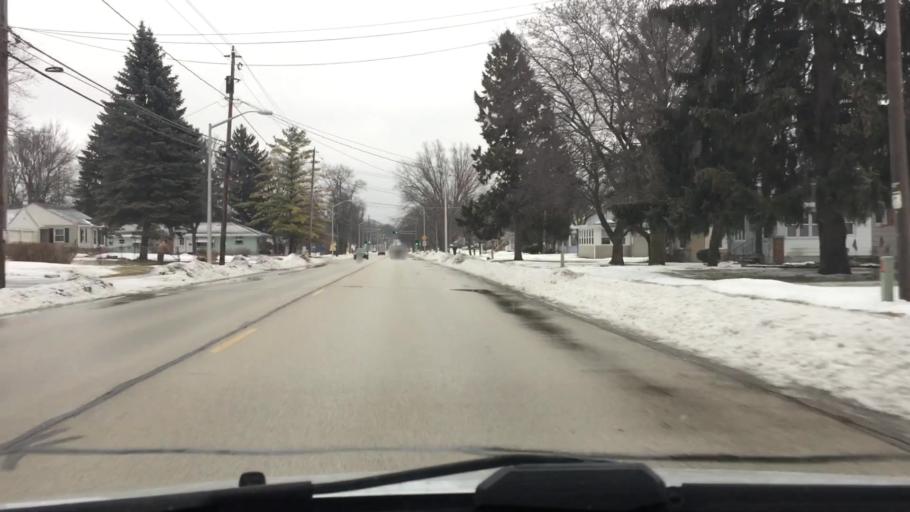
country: US
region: Wisconsin
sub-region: Waukesha County
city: Waukesha
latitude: 43.0284
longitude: -88.2560
